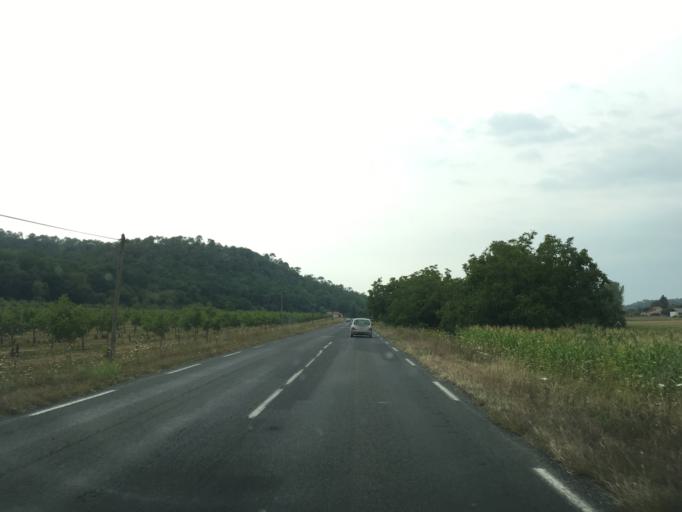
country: FR
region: Aquitaine
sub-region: Departement de la Dordogne
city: Carsac-Aillac
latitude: 44.8561
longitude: 1.3003
